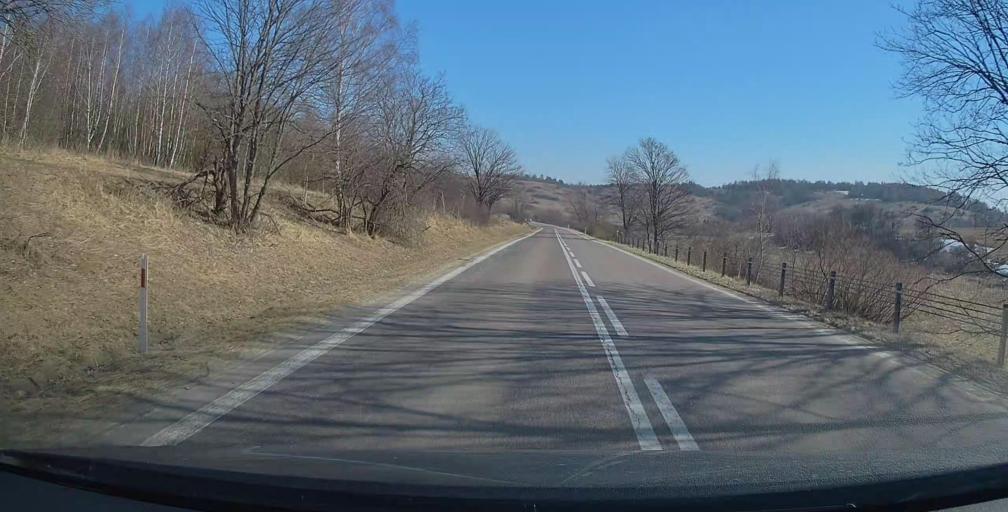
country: PL
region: Subcarpathian Voivodeship
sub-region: Powiat przemyski
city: Bircza
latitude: 49.5952
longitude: 22.4937
